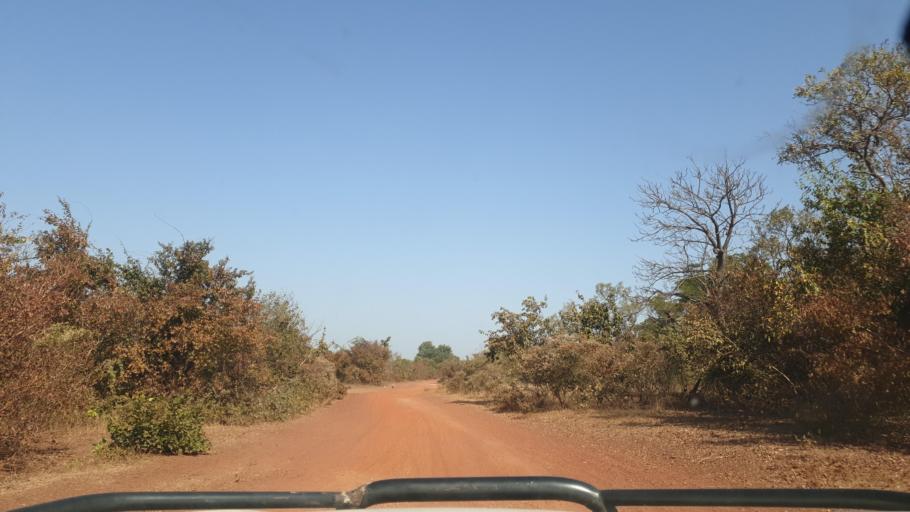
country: ML
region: Sikasso
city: Bougouni
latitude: 11.8312
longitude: -6.9786
